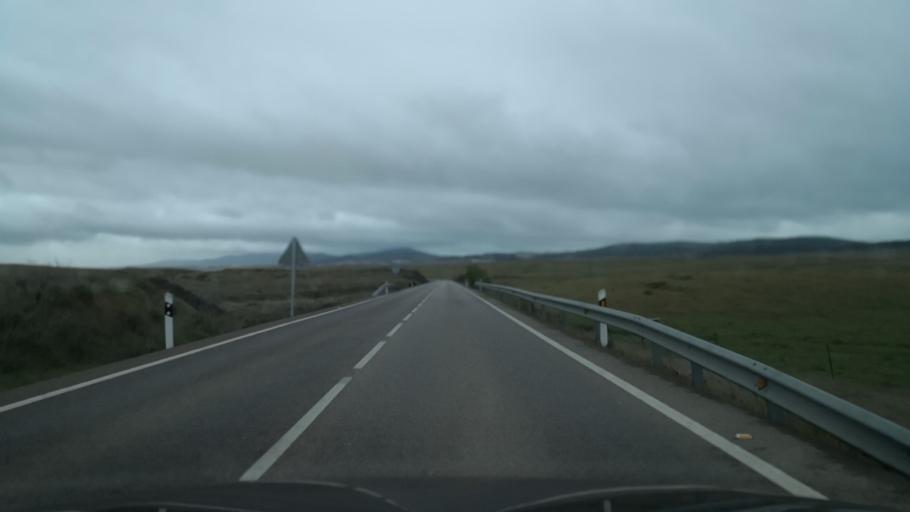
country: ES
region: Extremadura
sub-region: Provincia de Caceres
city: Casar de Caceres
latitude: 39.5334
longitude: -6.4053
